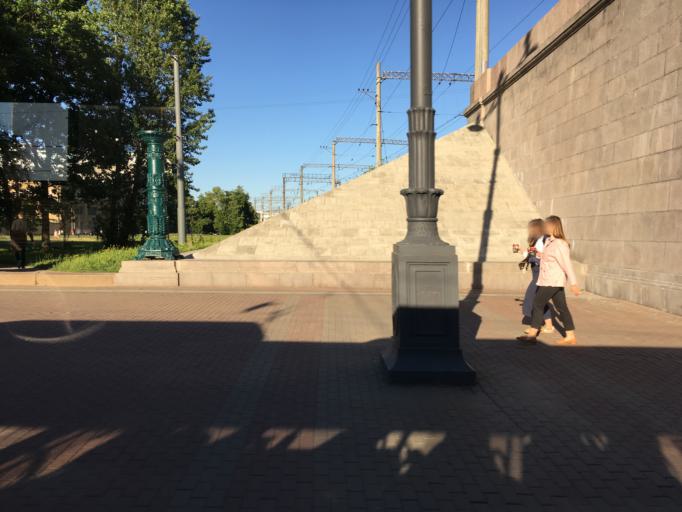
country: RU
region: St.-Petersburg
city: Admiralteisky
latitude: 59.8832
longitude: 30.3204
